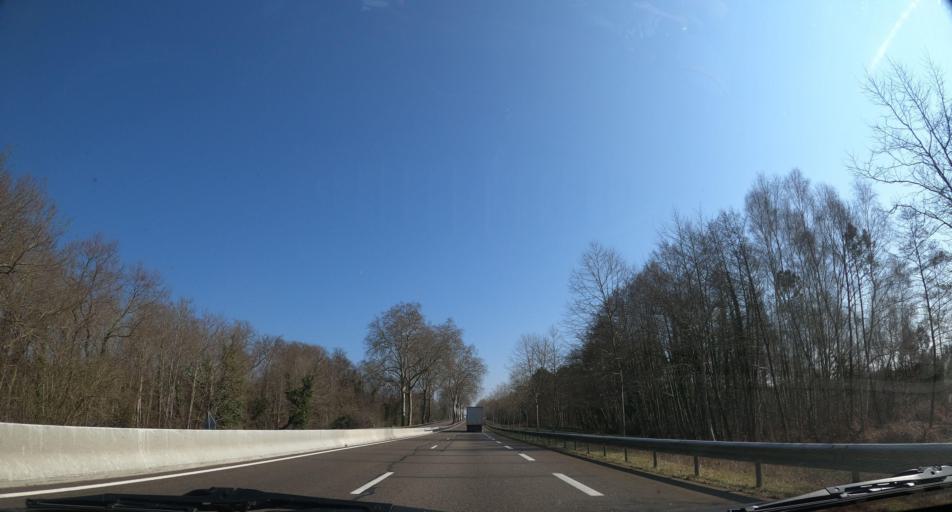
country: FR
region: Aquitaine
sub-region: Departement des Landes
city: Saint-Perdon
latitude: 43.8679
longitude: -0.6126
